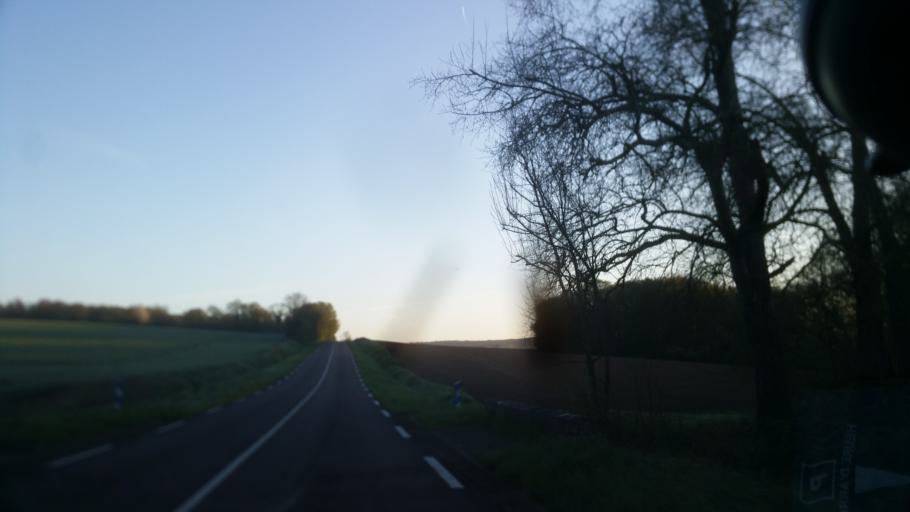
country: FR
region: Ile-de-France
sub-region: Departement de l'Essonne
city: Saint-Cyr-sous-Dourdan
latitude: 48.5586
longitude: 2.0275
